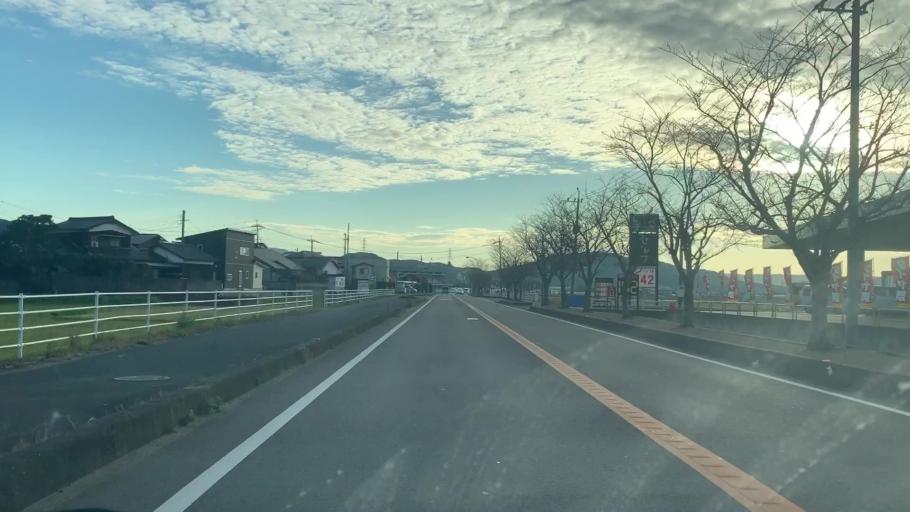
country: JP
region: Saga Prefecture
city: Karatsu
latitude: 33.4121
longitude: 129.9928
